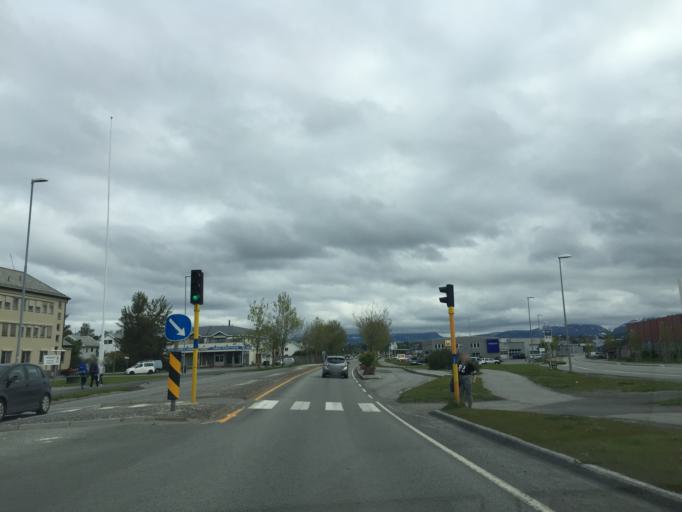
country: NO
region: Nordland
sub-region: Bodo
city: Bodo
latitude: 67.2847
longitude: 14.4077
